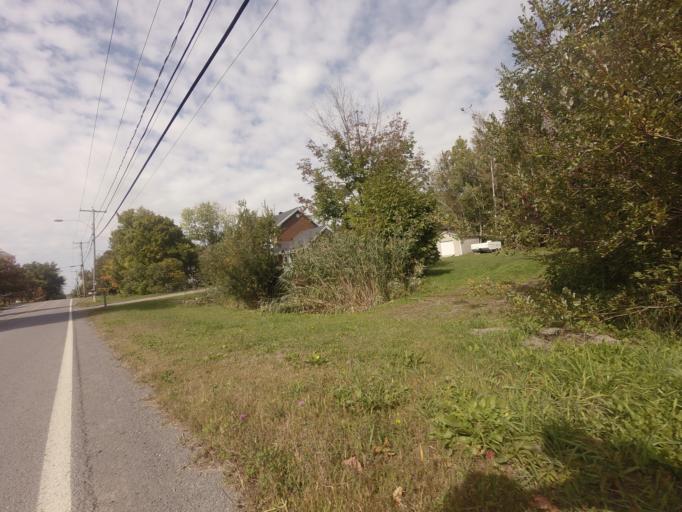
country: CA
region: Quebec
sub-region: Laurentides
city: Blainville
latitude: 45.6198
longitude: -73.9077
